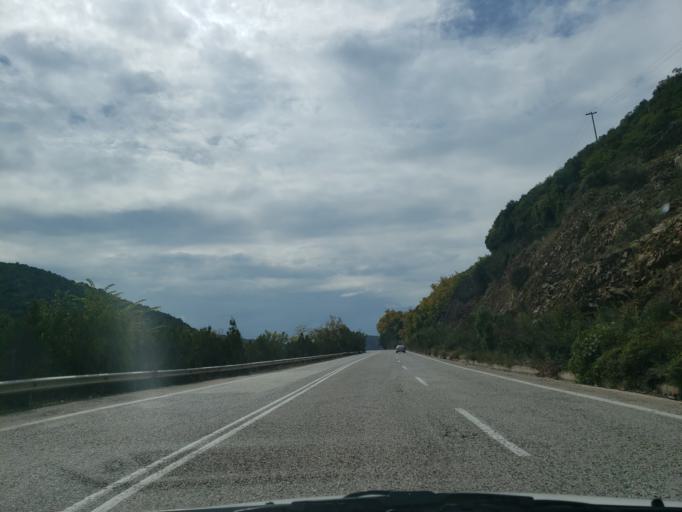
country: GR
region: Central Greece
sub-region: Nomos Fthiotidos
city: Stavros
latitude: 39.0116
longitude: 22.3774
